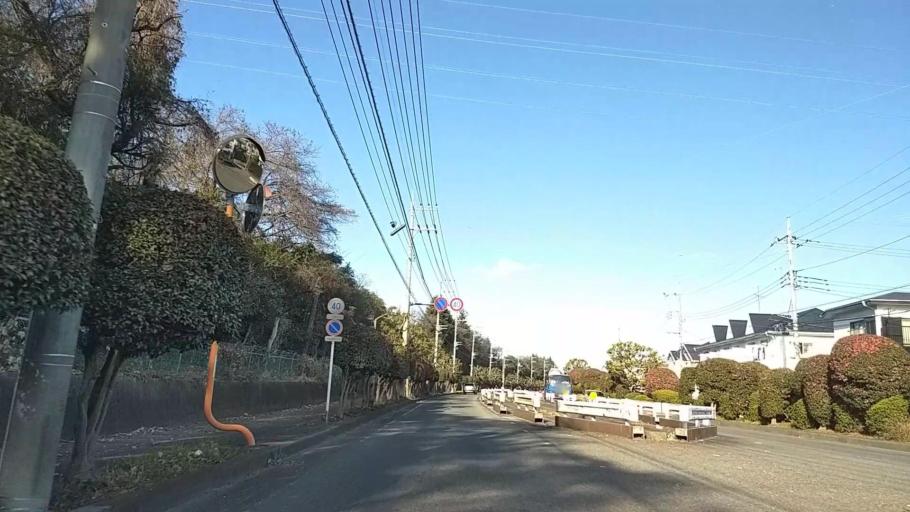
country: JP
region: Kanagawa
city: Atsugi
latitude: 35.4564
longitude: 139.3306
